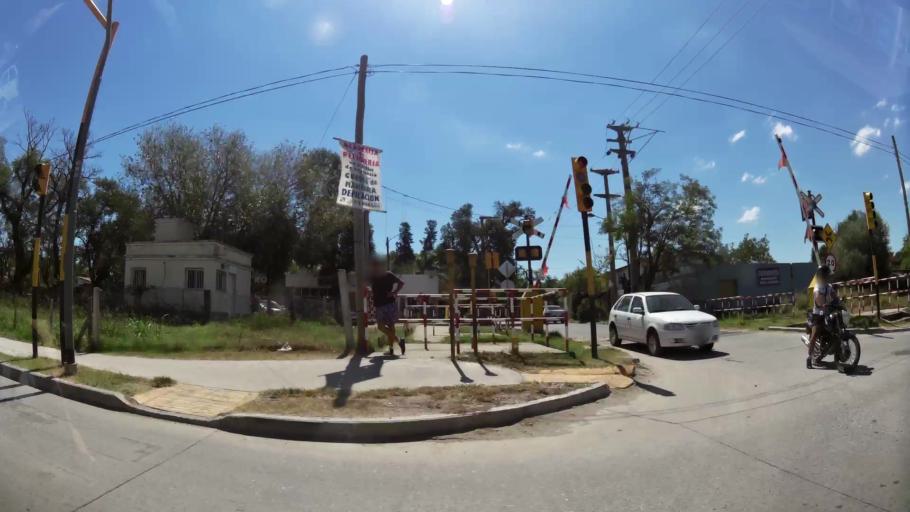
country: AR
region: Cordoba
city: Villa Allende
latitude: -31.3350
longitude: -64.2673
